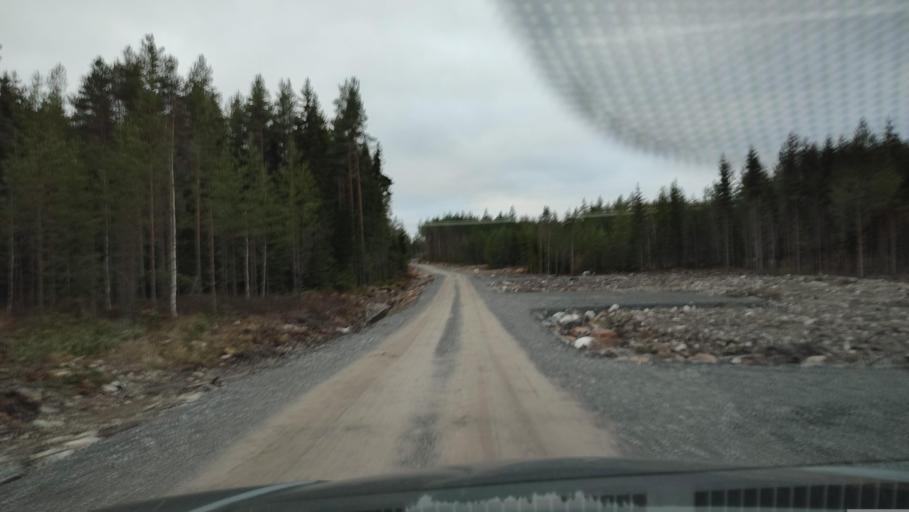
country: FI
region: Southern Ostrobothnia
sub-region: Suupohja
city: Karijoki
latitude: 62.2009
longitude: 21.5948
